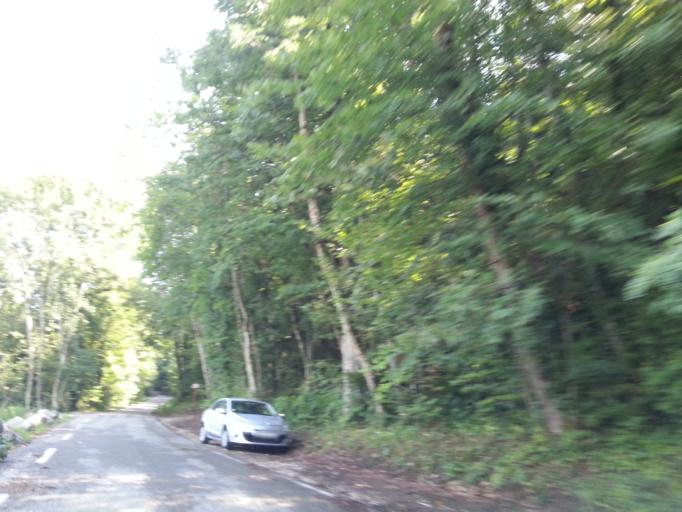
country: FR
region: Rhone-Alpes
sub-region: Departement de la Haute-Savoie
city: Annecy-le-Vieux
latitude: 45.9157
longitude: 6.1711
